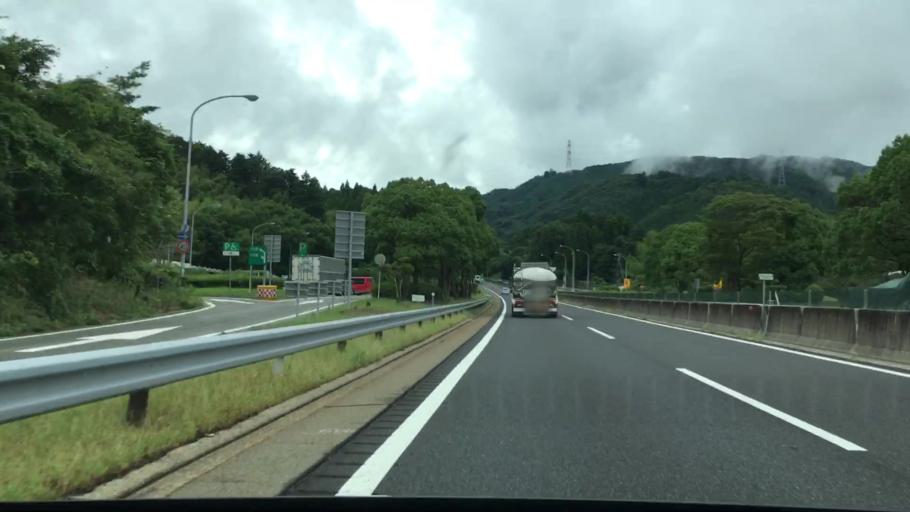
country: JP
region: Hyogo
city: Yamazakicho-nakabirose
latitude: 35.0306
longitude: 134.4868
